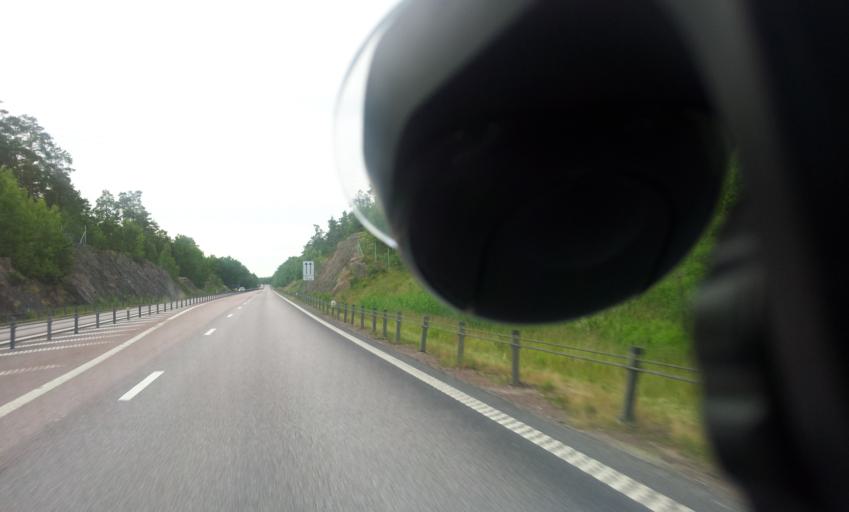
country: SE
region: Kalmar
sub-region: Oskarshamns Kommun
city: Paskallavik
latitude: 57.1780
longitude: 16.4445
